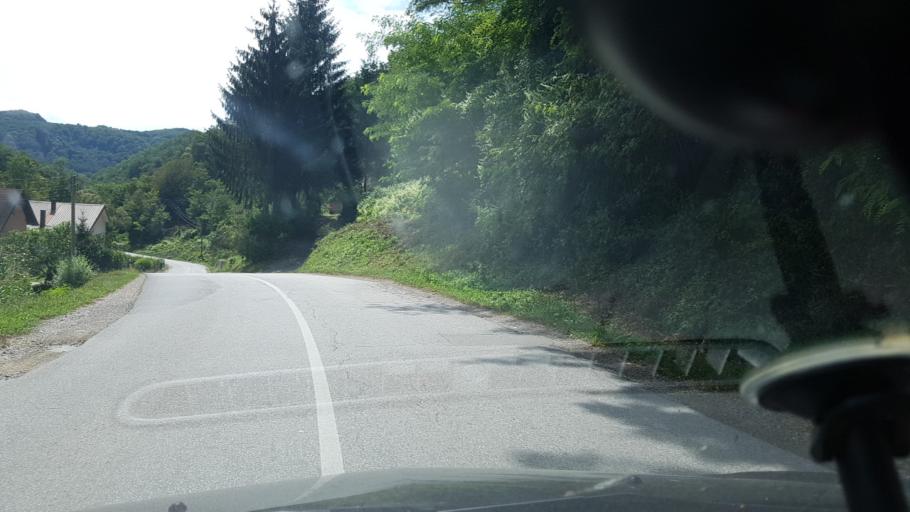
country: HR
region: Krapinsko-Zagorska
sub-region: Grad Krapina
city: Krapina
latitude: 46.1916
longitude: 15.8587
